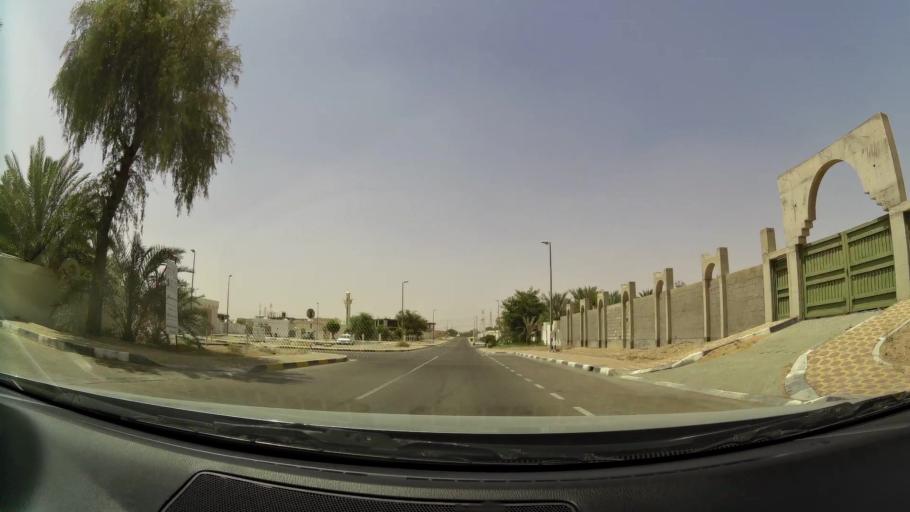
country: OM
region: Al Buraimi
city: Al Buraymi
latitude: 24.2652
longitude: 55.7063
